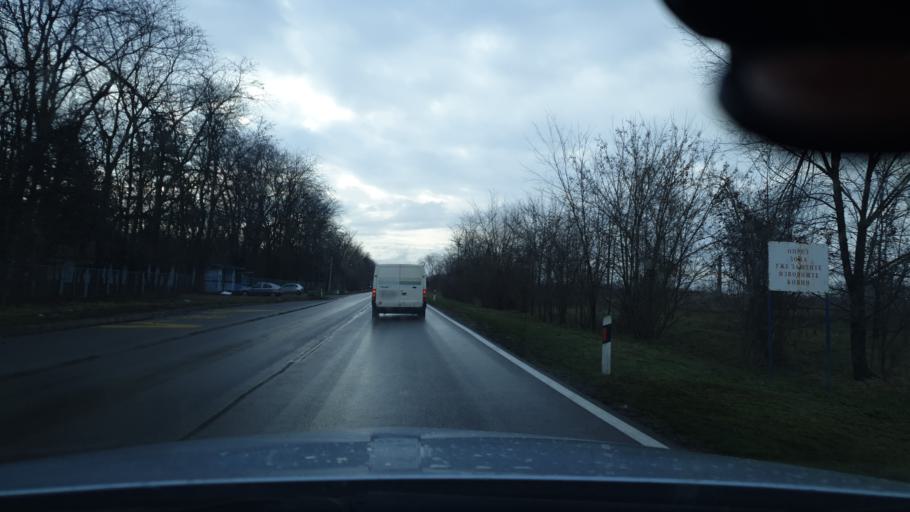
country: RS
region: Autonomna Pokrajina Vojvodina
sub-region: Juznobanatski Okrug
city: Kovin
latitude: 44.7579
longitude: 20.9622
